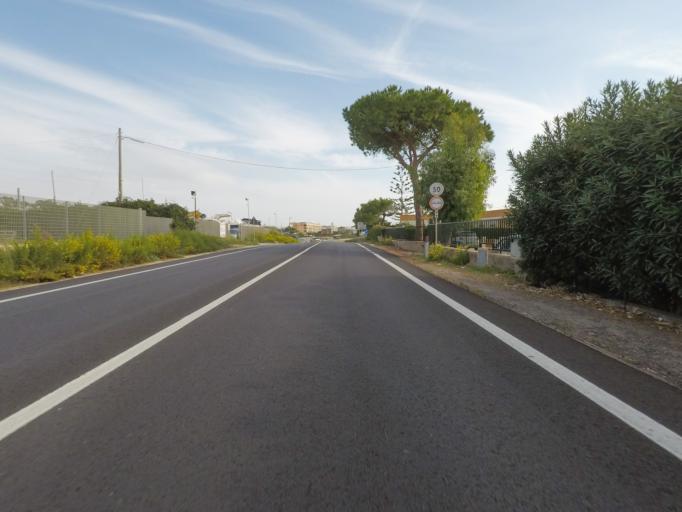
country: IT
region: Latium
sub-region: Citta metropolitana di Roma Capitale
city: Santa Marinella
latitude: 42.0460
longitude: 11.8243
